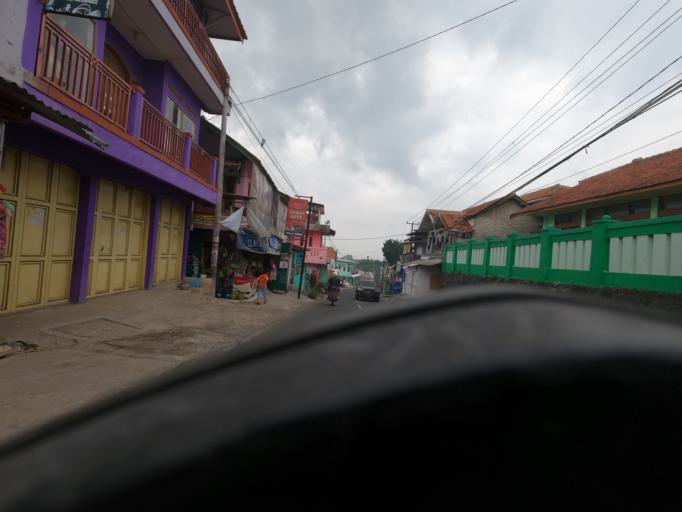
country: ID
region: West Java
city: Lembang
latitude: -6.8078
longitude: 107.5696
